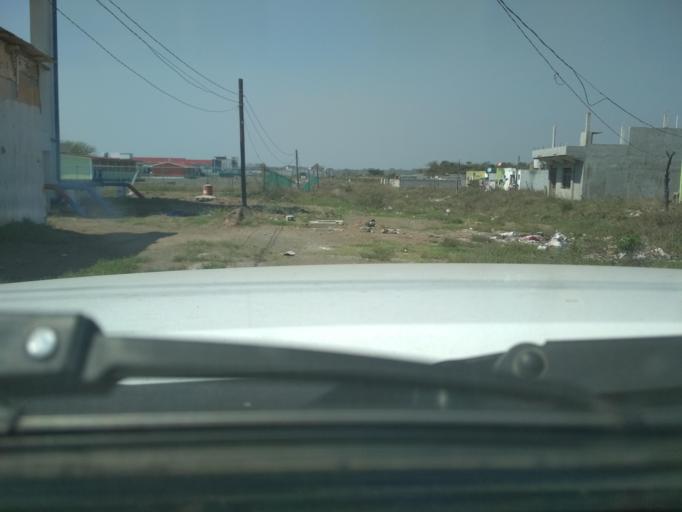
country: MX
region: Veracruz
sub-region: Veracruz
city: Lomas de Rio Medio Cuatro
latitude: 19.1944
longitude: -96.1973
